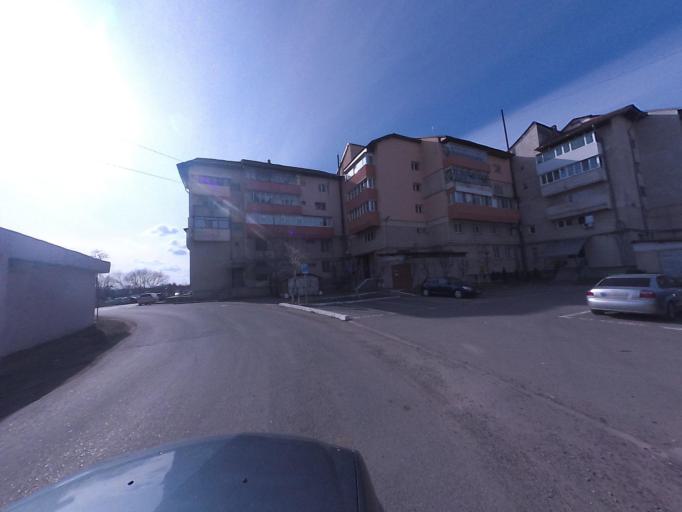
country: RO
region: Neamt
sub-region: Oras Targu Neamt
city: Humulesti
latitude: 47.2015
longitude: 26.3591
